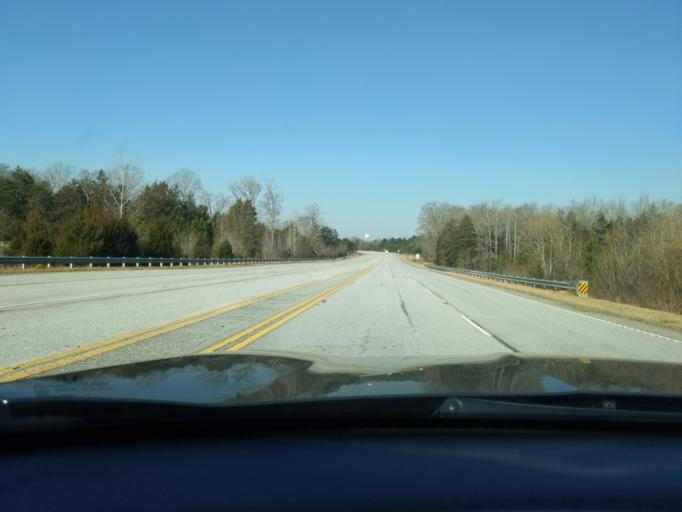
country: US
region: South Carolina
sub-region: Abbeville County
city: Calhoun Falls
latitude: 34.0954
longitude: -82.5731
